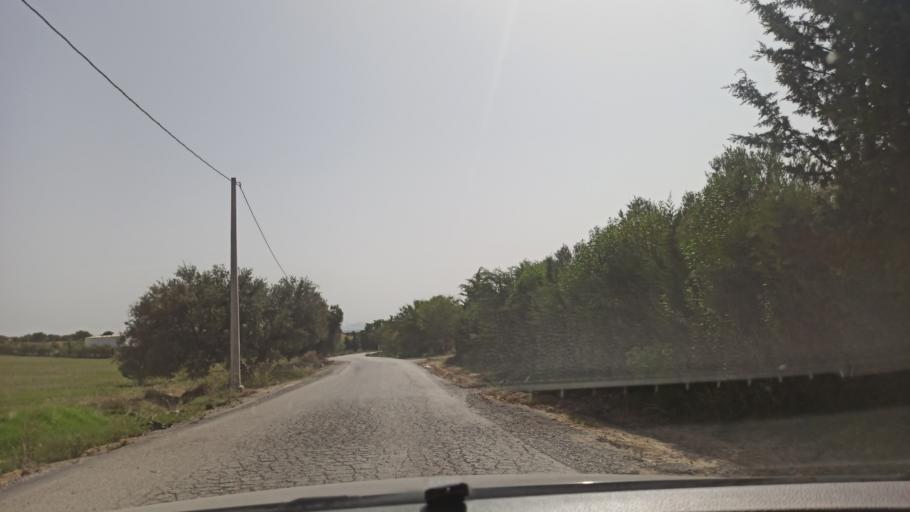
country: TN
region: Manouba
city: Manouba
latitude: 36.7318
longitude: 10.0939
